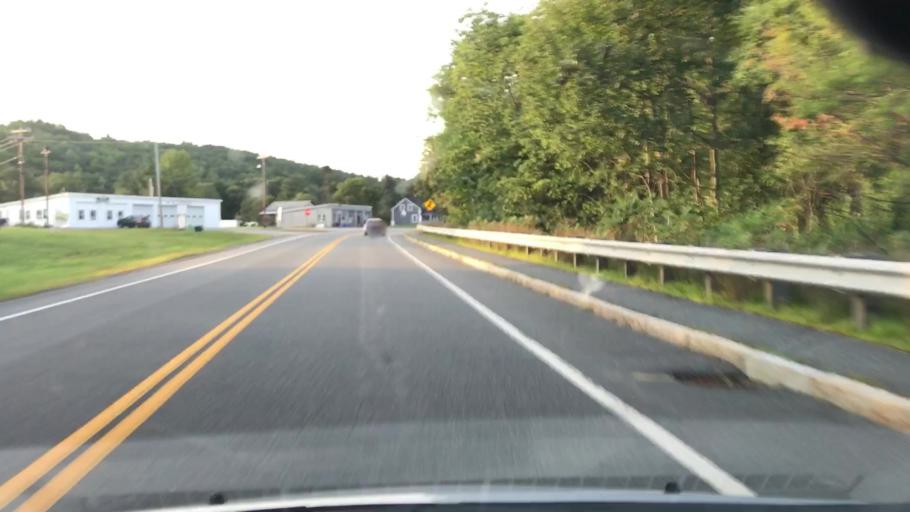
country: US
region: New Hampshire
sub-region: Grafton County
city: Rumney
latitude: 43.9246
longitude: -71.8906
